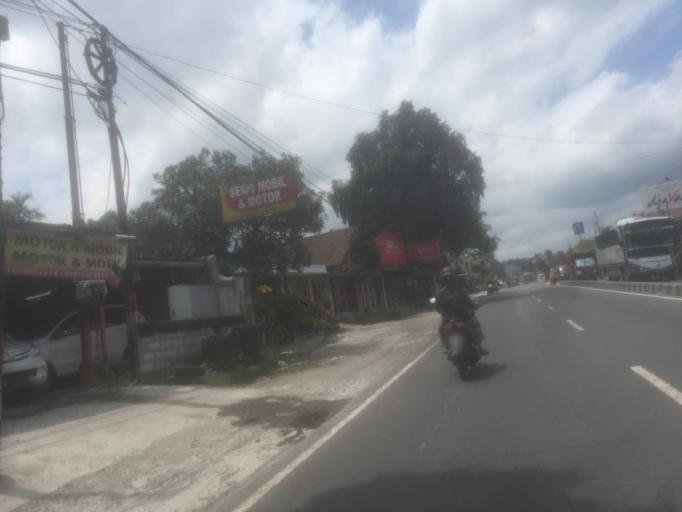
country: ID
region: Central Java
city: Muntilan
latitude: -7.6264
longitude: 110.3170
